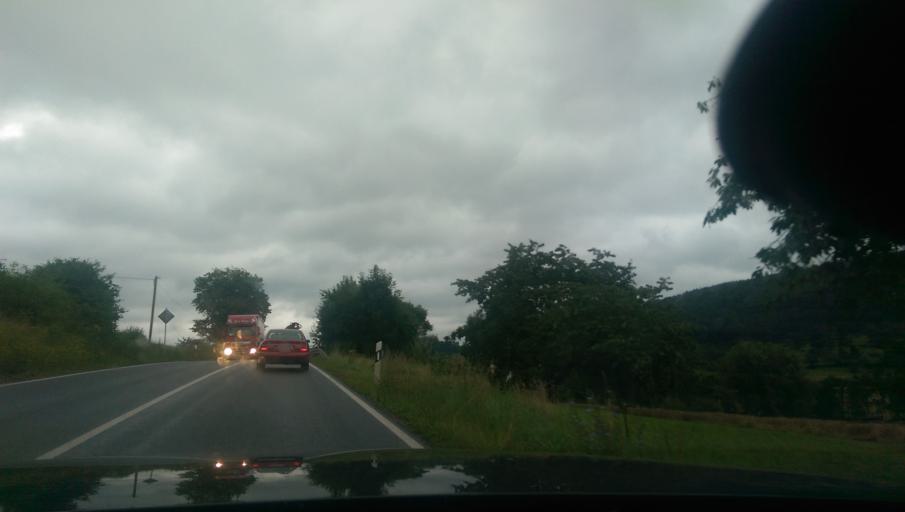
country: DE
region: Hesse
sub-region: Regierungsbezirk Kassel
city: Grossalmerode
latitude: 51.2798
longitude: 9.8424
